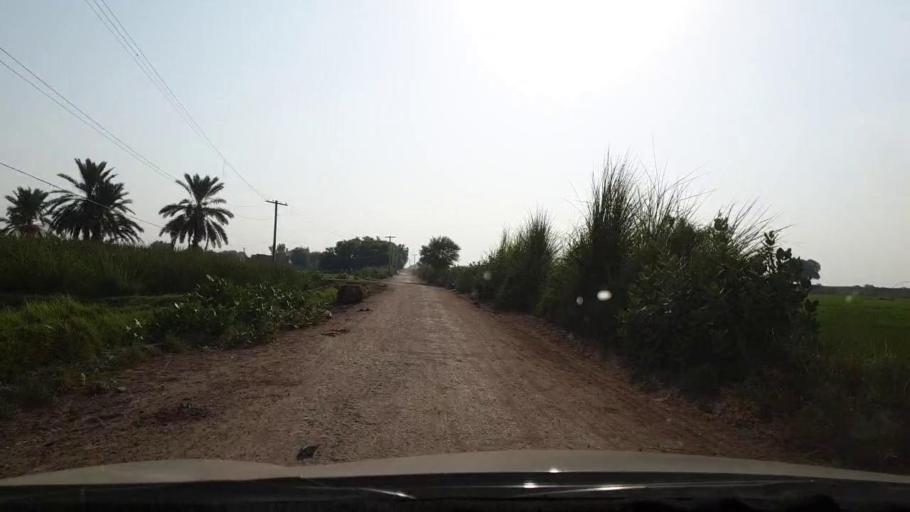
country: PK
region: Sindh
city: Larkana
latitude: 27.5531
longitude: 68.2679
